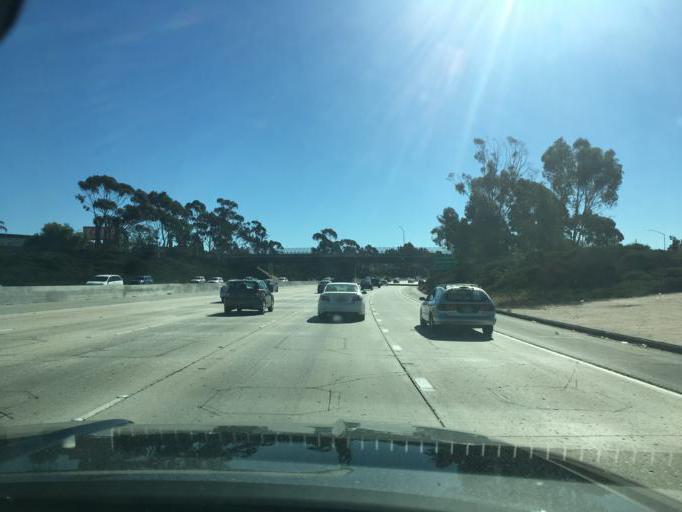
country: US
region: California
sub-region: San Diego County
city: National City
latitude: 32.7060
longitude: -117.0960
